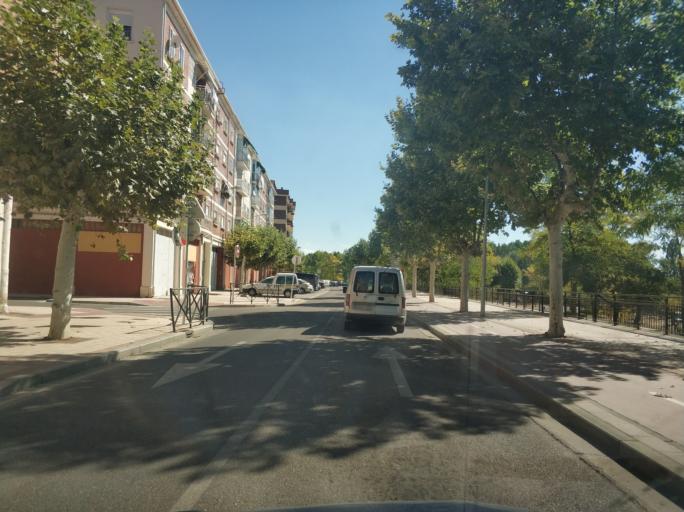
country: ES
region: Castille and Leon
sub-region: Provincia de Burgos
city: Aranda de Duero
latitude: 41.6691
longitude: -3.6803
